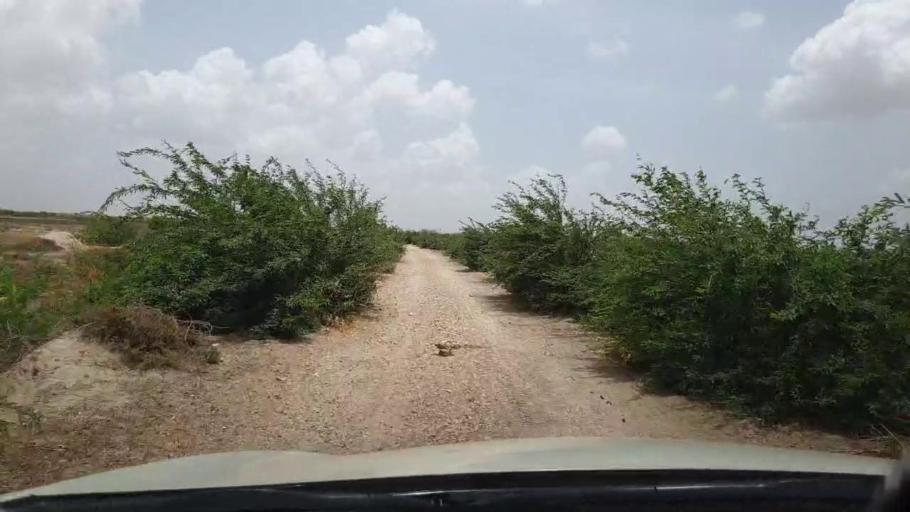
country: PK
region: Sindh
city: Kadhan
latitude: 24.3535
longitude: 68.9235
